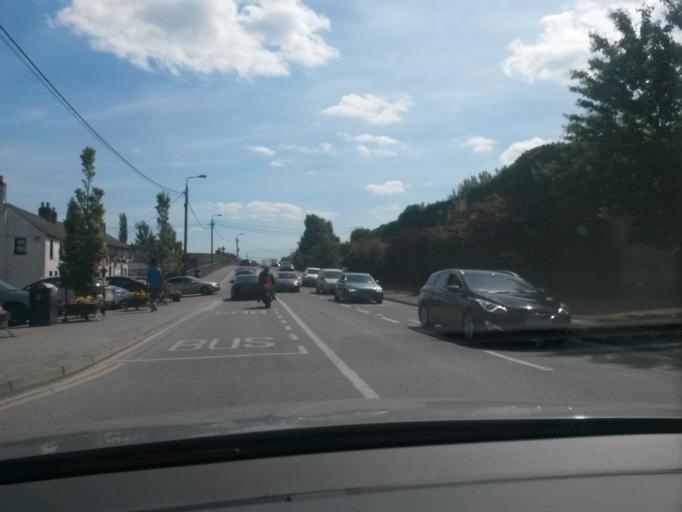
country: IE
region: Leinster
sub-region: Kildare
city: Sallins
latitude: 53.2501
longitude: -6.6652
